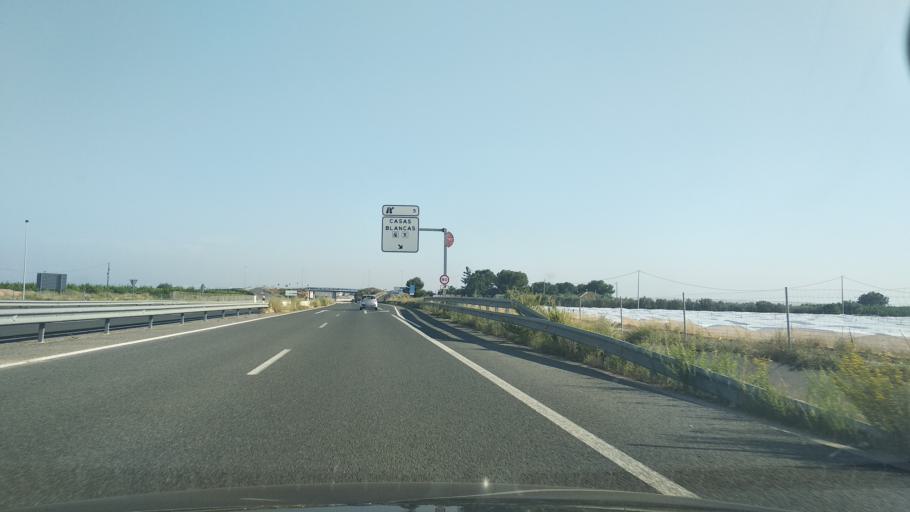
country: ES
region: Murcia
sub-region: Murcia
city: San Javier
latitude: 37.8524
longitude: -0.8806
